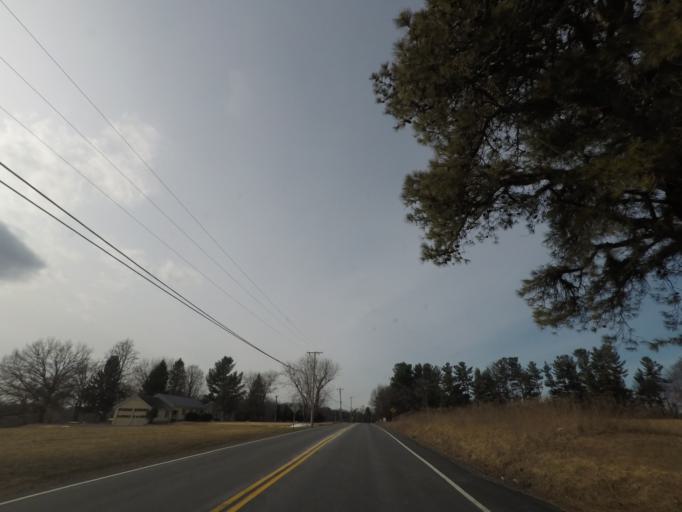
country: US
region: New York
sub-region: Columbia County
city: Valatie
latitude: 42.4009
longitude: -73.6674
